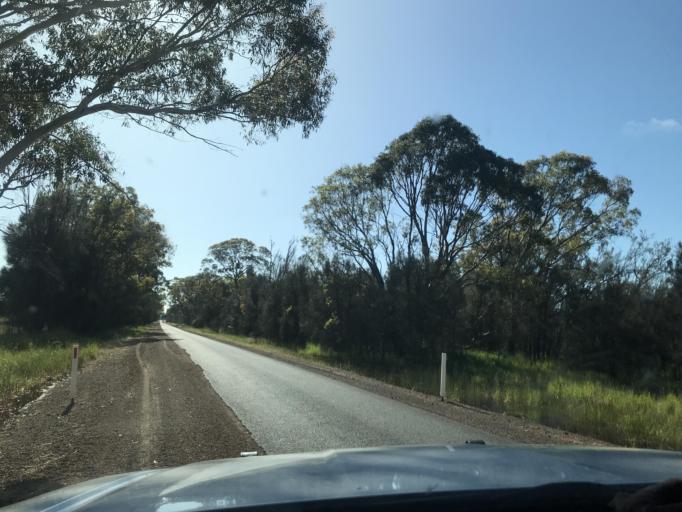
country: AU
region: Victoria
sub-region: Horsham
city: Horsham
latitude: -37.0055
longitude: 141.6256
